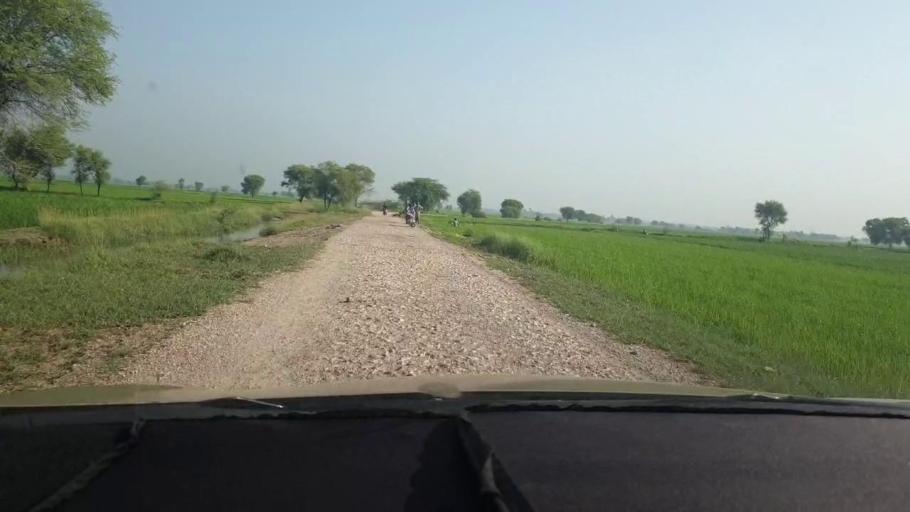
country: PK
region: Sindh
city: Kambar
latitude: 27.5860
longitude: 68.1025
